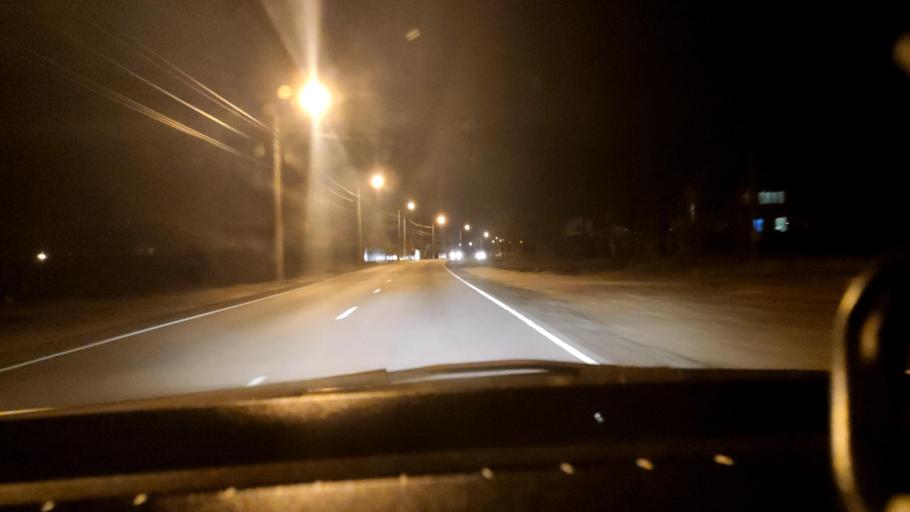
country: RU
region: Voronezj
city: Shilovo
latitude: 51.5503
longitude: 39.0804
